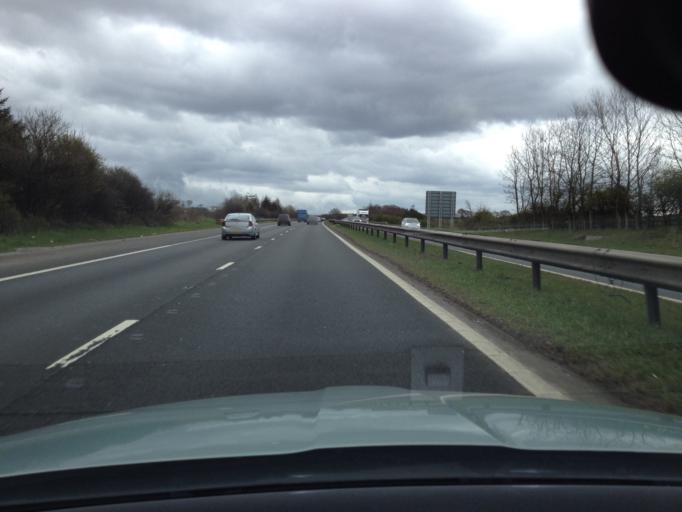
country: GB
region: Scotland
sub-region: North Lanarkshire
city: Cleland
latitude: 55.8428
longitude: -3.9006
